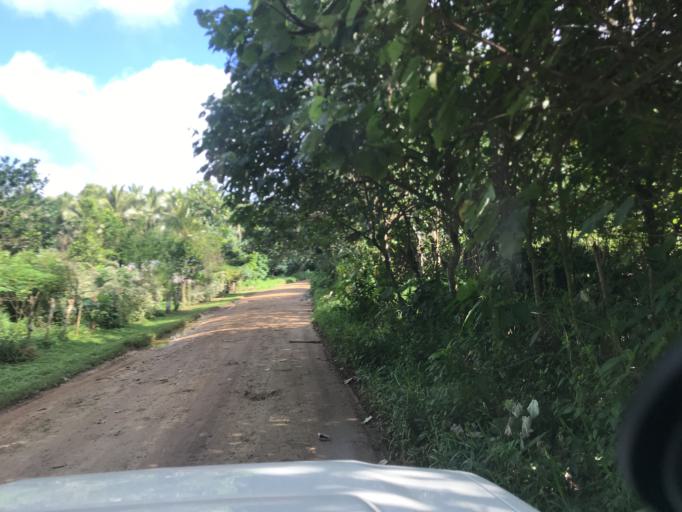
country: VU
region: Sanma
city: Luganville
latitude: -15.5087
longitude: 167.1071
